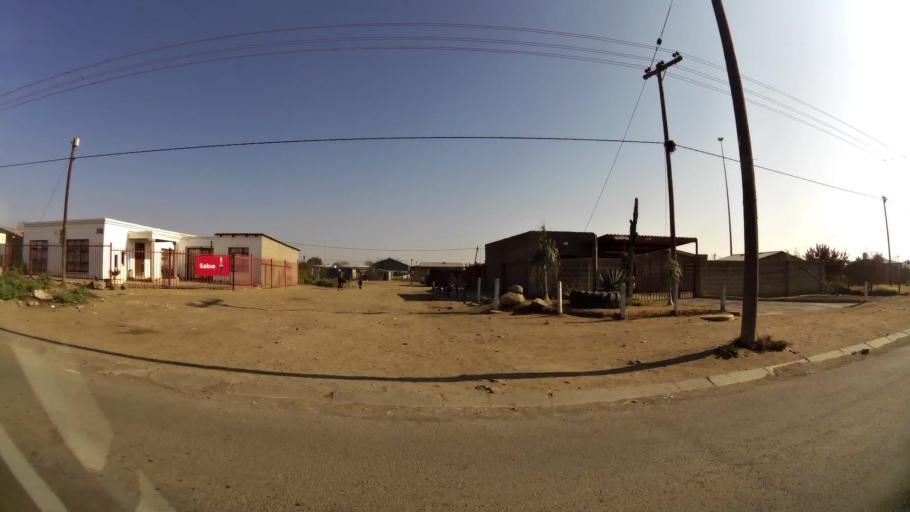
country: ZA
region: Orange Free State
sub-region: Mangaung Metropolitan Municipality
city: Bloemfontein
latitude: -29.1718
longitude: 26.2311
